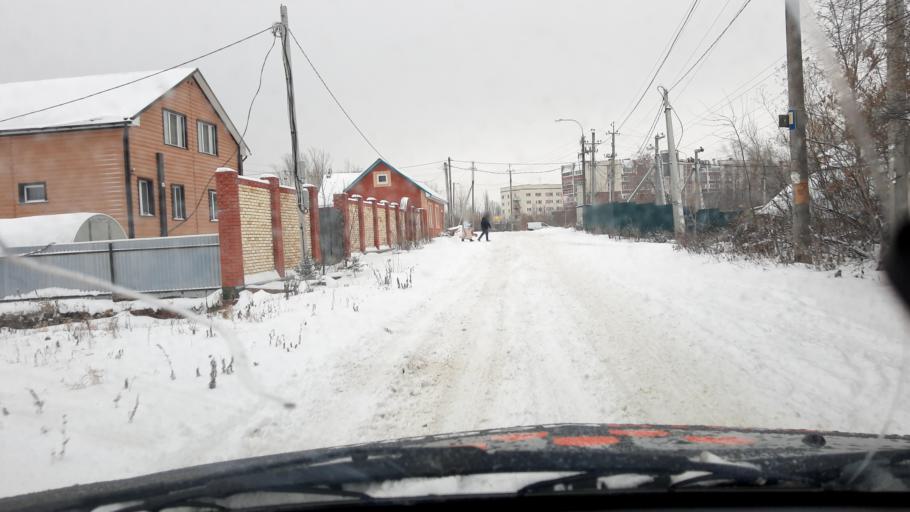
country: RU
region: Bashkortostan
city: Ufa
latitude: 54.6680
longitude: 55.9398
